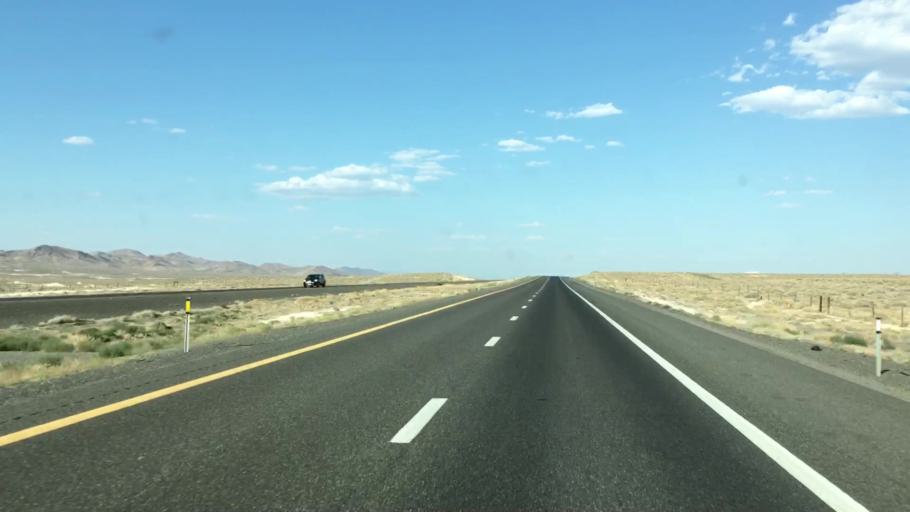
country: US
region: Nevada
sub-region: Lyon County
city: Fernley
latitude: 39.8339
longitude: -118.9598
